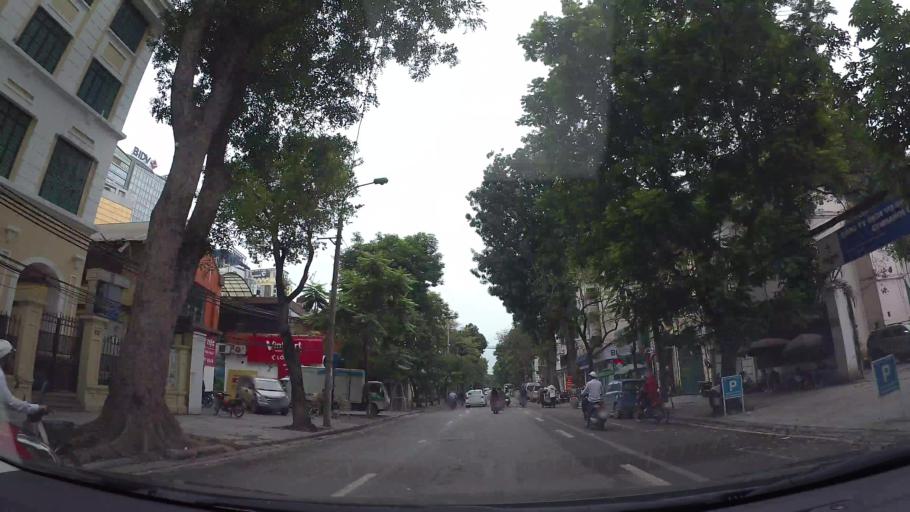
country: VN
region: Ha Noi
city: Hoan Kiem
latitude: 21.0302
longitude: 105.8551
